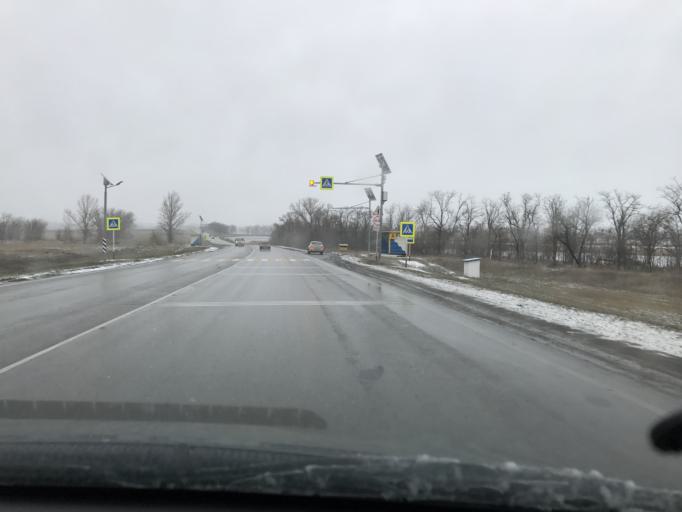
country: RU
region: Rostov
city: Mechetinskaya
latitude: 46.6736
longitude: 40.5291
